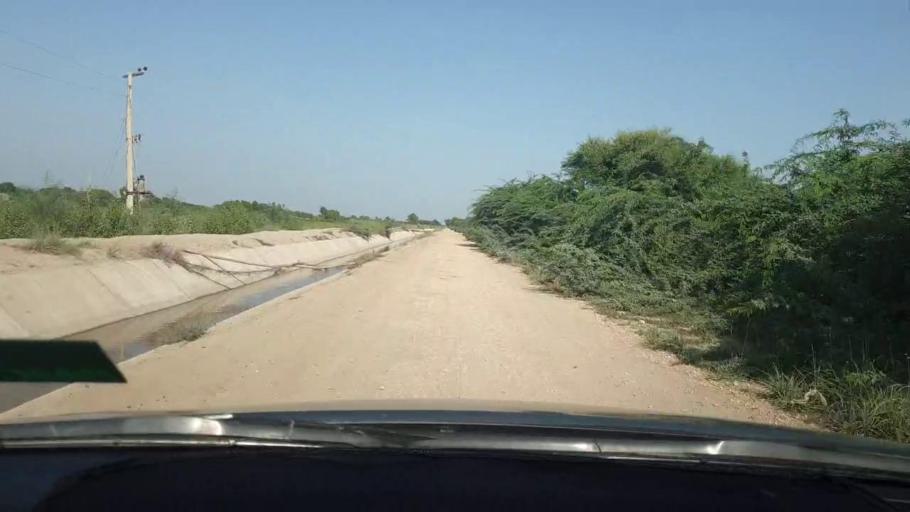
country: PK
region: Sindh
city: Naukot
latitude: 24.9300
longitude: 69.2653
